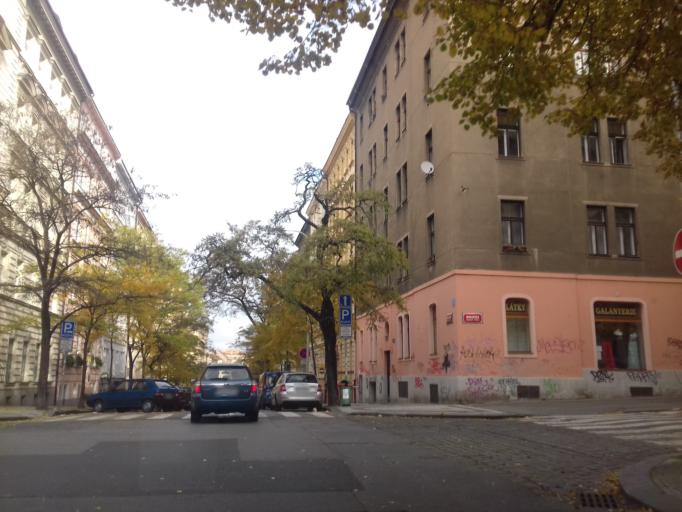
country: CZ
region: Praha
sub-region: Praha 8
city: Karlin
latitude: 50.0743
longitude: 14.4420
